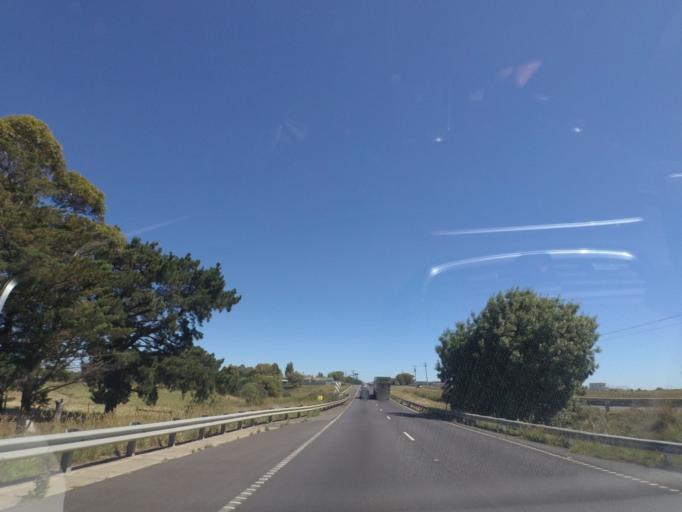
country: AU
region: Victoria
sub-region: Hume
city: Craigieburn
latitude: -37.5276
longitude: 144.9478
